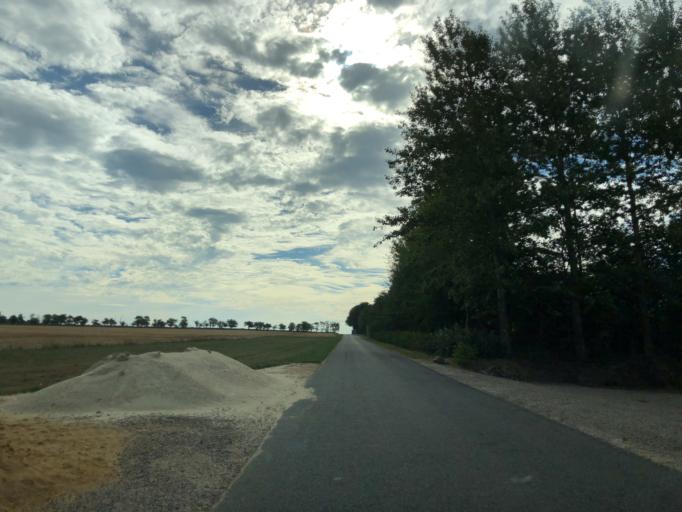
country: DK
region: Central Jutland
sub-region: Ringkobing-Skjern Kommune
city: Skjern
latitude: 56.0434
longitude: 8.4281
